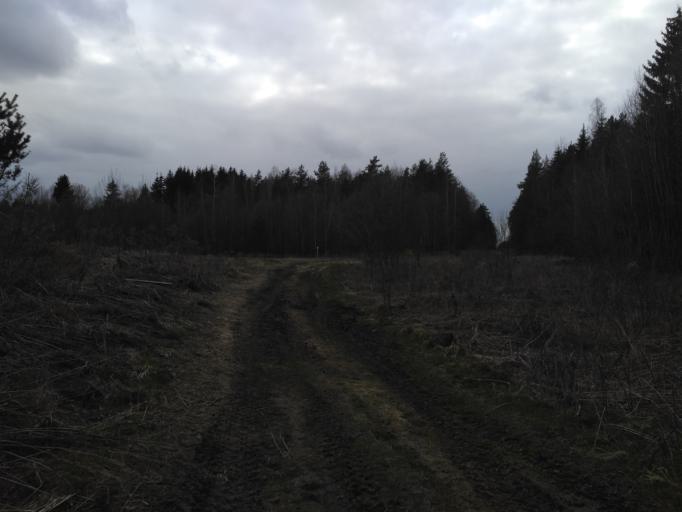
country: BY
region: Minsk
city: Korolev Stan
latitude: 54.0099
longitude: 27.8160
